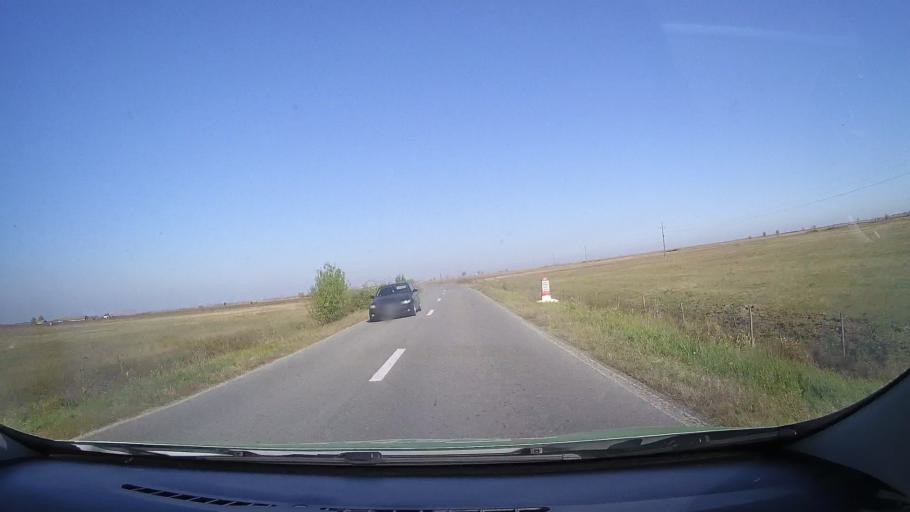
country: RO
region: Satu Mare
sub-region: Comuna Cauas
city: Cauas
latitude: 47.5449
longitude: 22.5628
